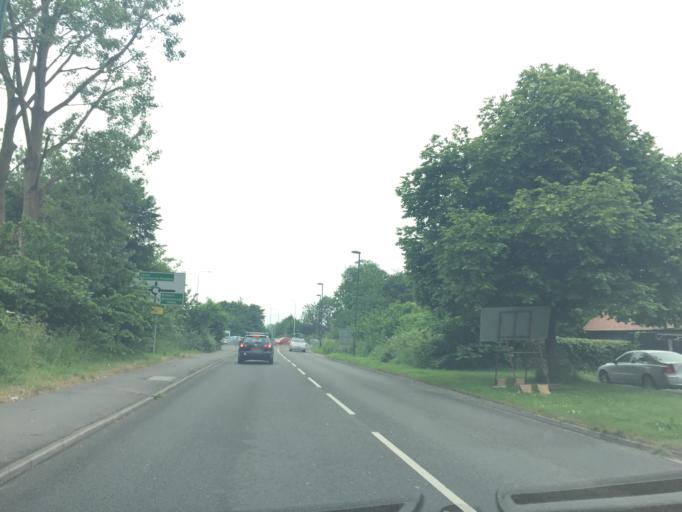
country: GB
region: England
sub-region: Dorset
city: Dorchester
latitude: 50.7014
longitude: -2.4463
